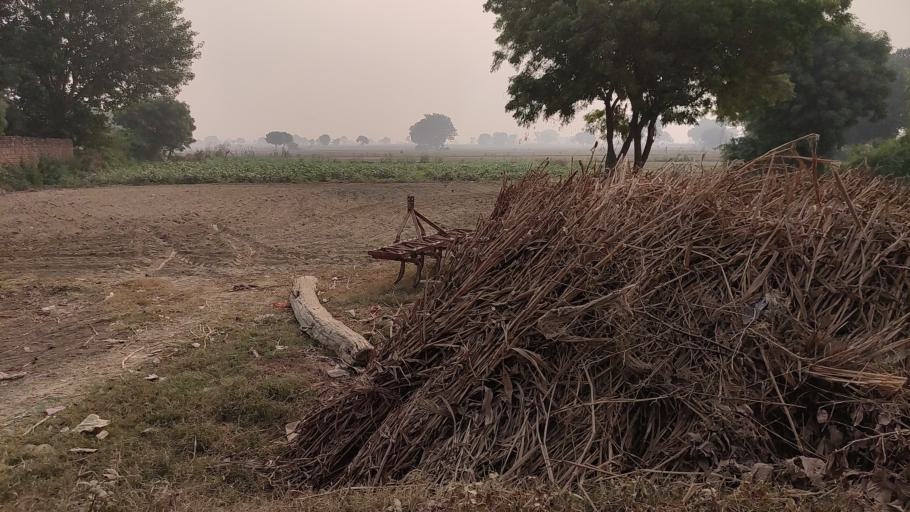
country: IN
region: Uttar Pradesh
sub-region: Mathura
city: Vrindavan
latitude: 27.5445
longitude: 77.7106
